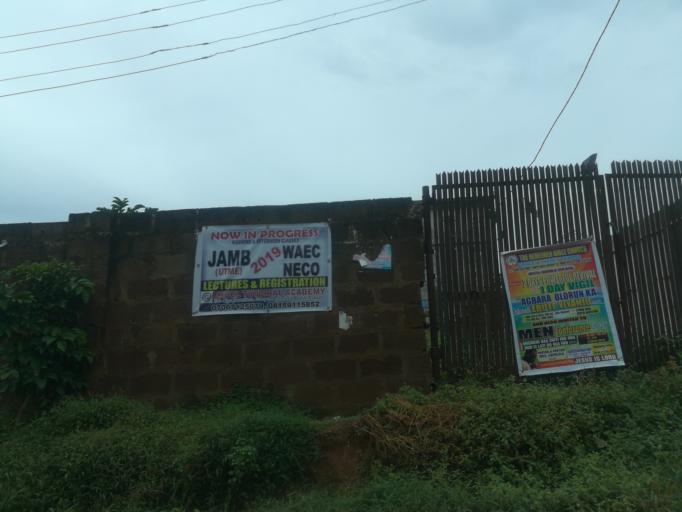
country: NG
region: Oyo
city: Ibadan
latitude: 7.3368
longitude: 3.9006
